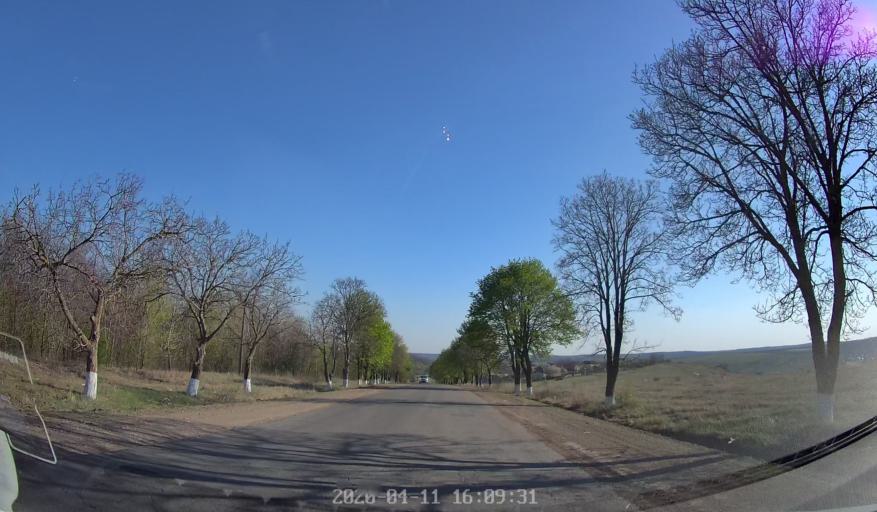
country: MD
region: Chisinau
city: Vadul lui Voda
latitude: 47.0735
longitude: 29.1366
